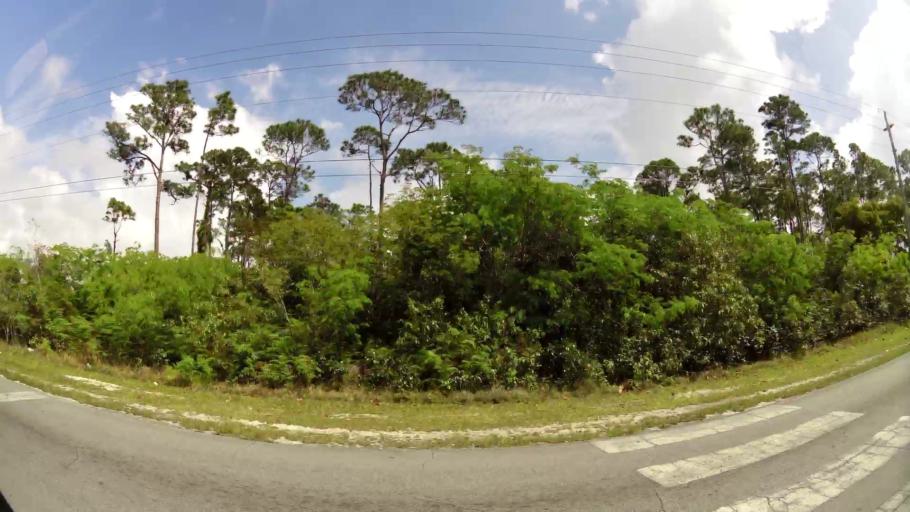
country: BS
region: Freeport
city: Freeport
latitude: 26.5077
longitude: -78.6911
